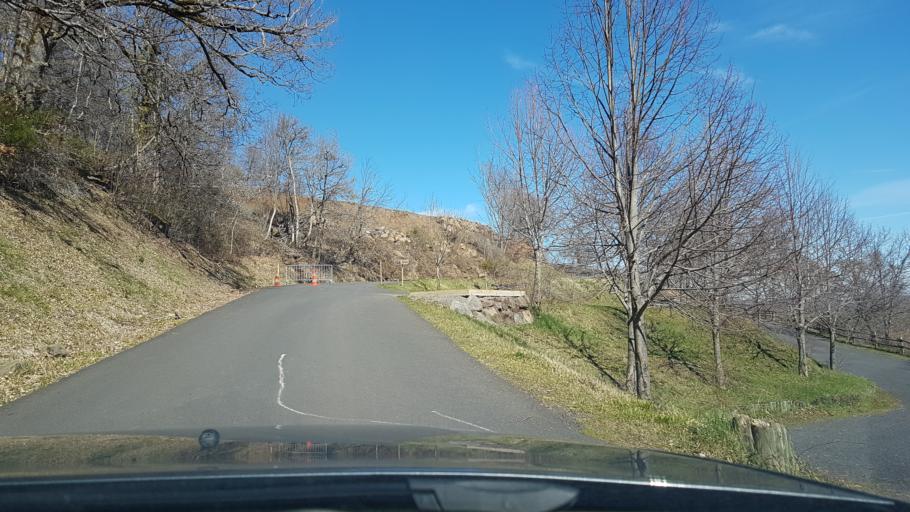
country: FR
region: Auvergne
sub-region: Departement du Puy-de-Dome
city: Aydat
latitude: 45.5405
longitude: 2.9916
